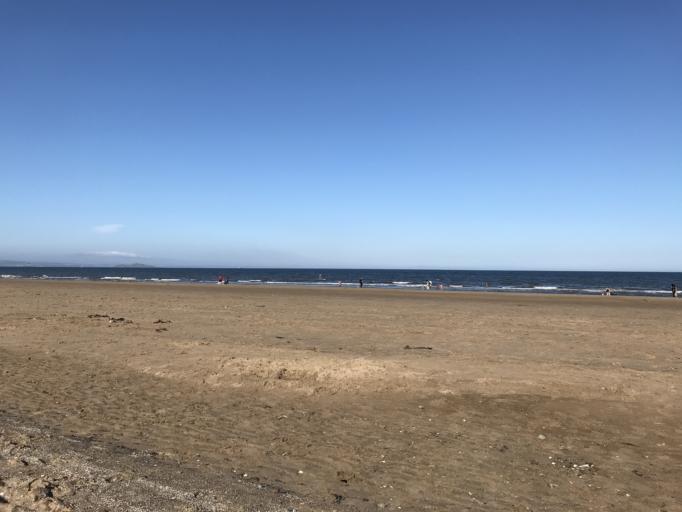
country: GB
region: Scotland
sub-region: West Lothian
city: Seafield
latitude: 55.9589
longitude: -3.1191
